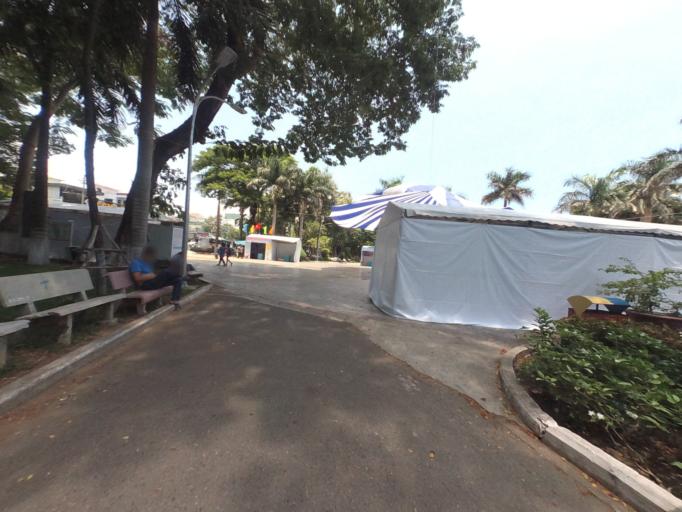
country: VN
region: Da Nang
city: Thanh Khe
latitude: 16.0623
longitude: 108.2046
